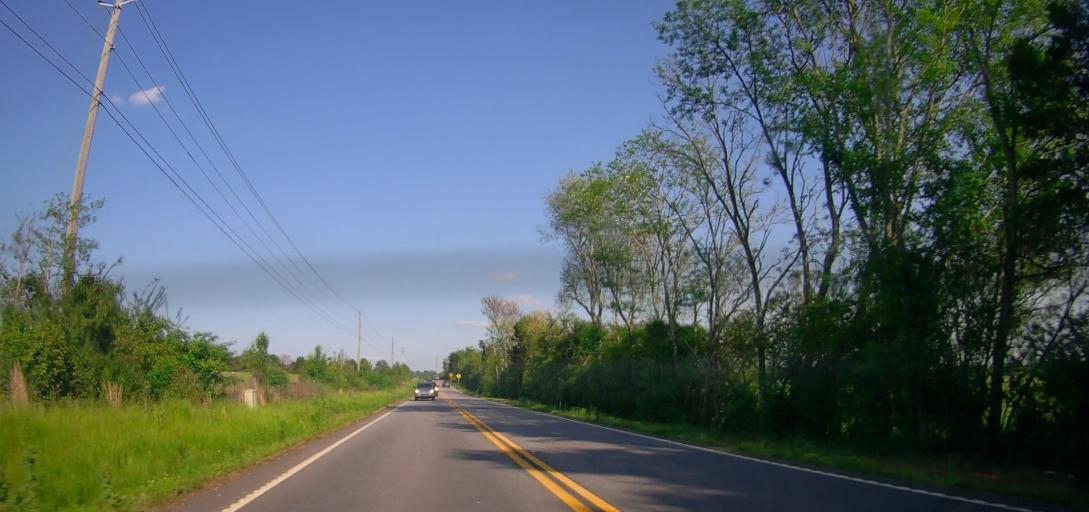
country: US
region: Georgia
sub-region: Walton County
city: Social Circle
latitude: 33.5970
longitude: -83.7691
